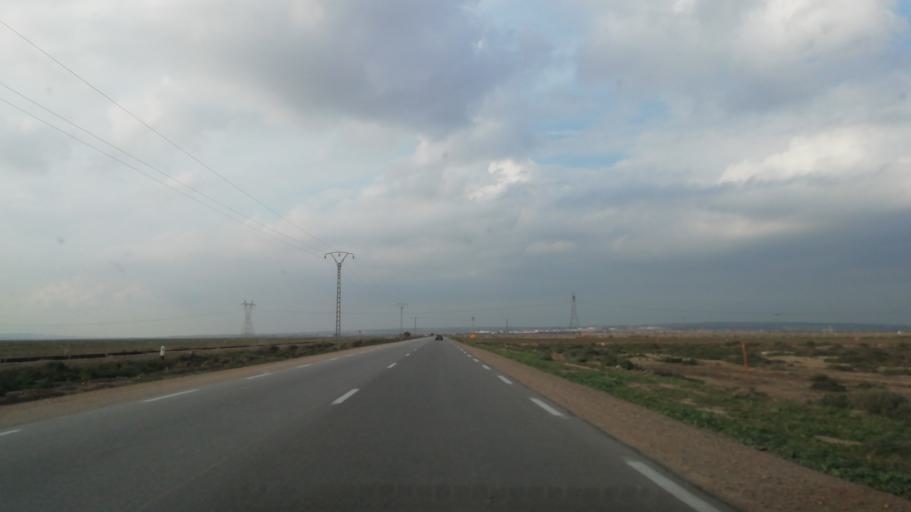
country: DZ
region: Mascara
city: Sig
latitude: 35.6996
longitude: -0.0245
